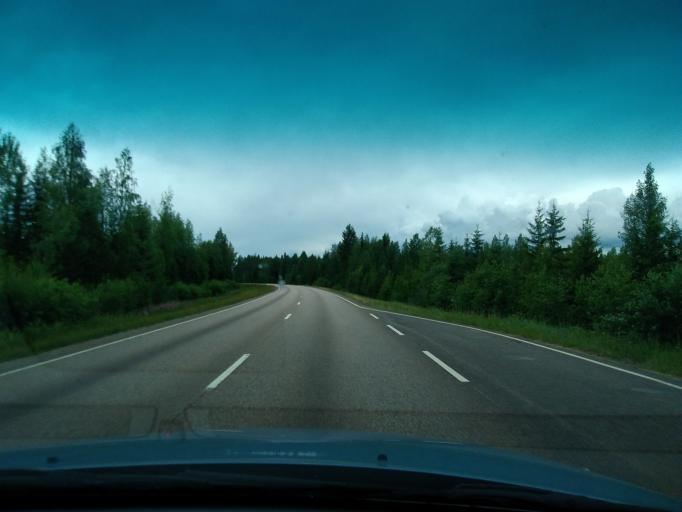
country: FI
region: Central Finland
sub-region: Keuruu
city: Multia
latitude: 62.3862
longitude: 24.7569
